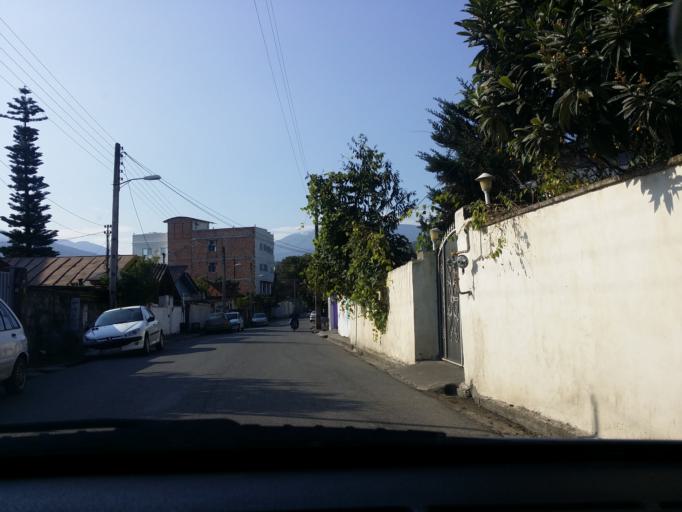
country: IR
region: Mazandaran
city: Chalus
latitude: 36.6534
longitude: 51.4145
